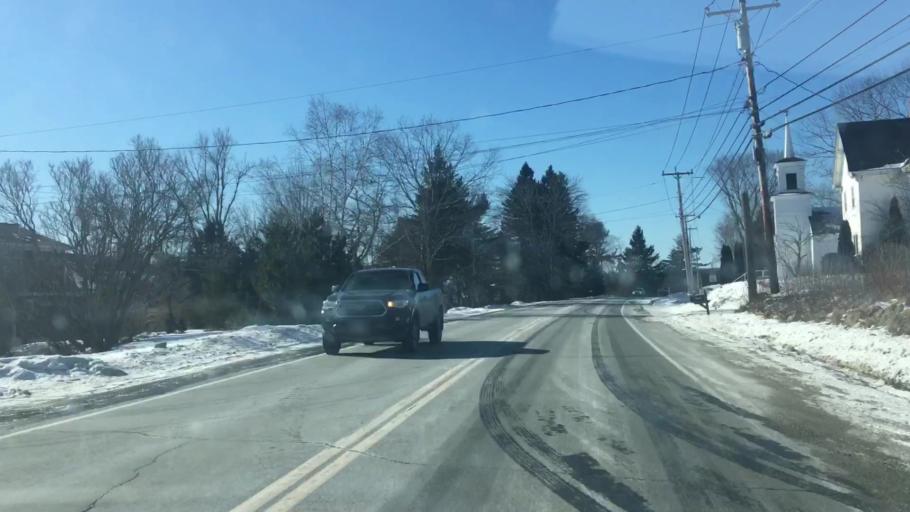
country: US
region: Maine
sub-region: Hancock County
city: Surry
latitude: 44.4962
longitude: -68.4958
